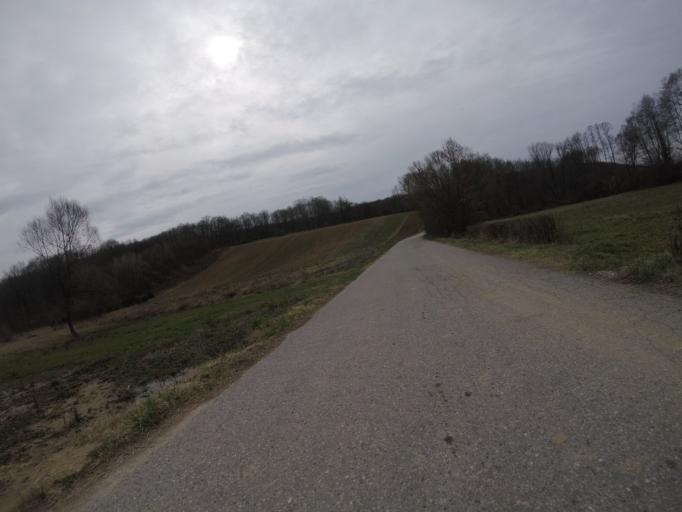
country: HR
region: Grad Zagreb
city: Strmec
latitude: 45.5867
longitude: 15.9504
